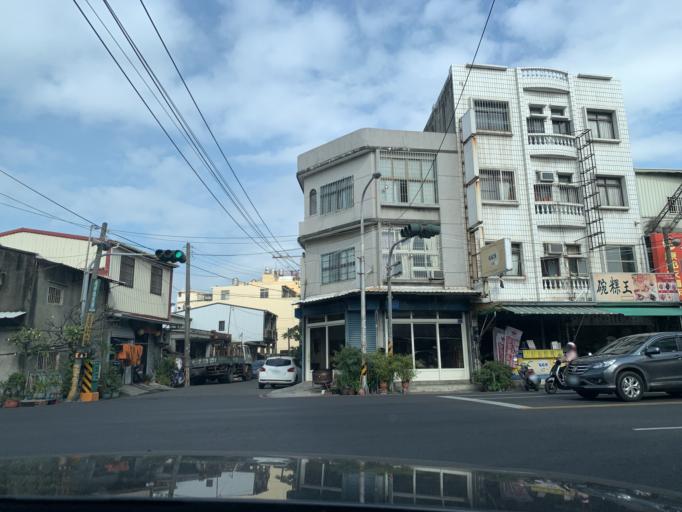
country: TW
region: Taiwan
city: Fengshan
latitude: 22.4679
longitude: 120.4476
